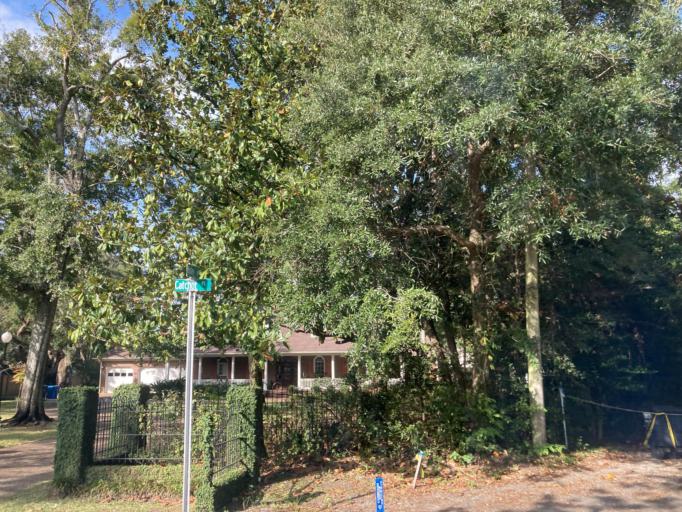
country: US
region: Mississippi
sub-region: Jackson County
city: Ocean Springs
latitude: 30.4131
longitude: -88.8320
